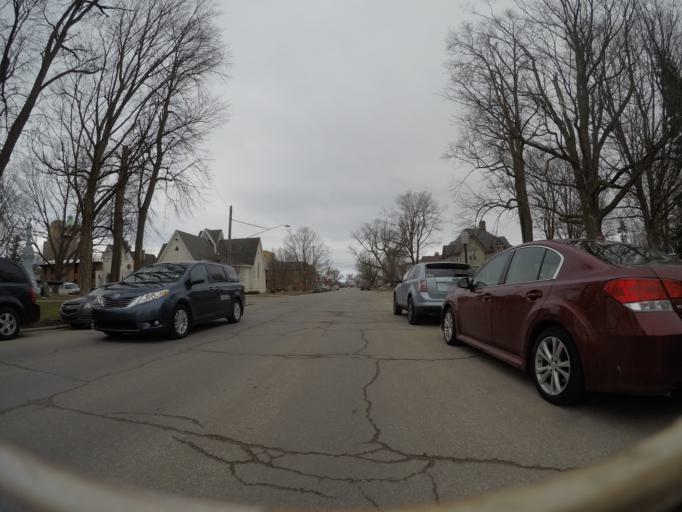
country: US
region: Michigan
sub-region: Grand Traverse County
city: Traverse City
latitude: 44.7615
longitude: -85.6158
